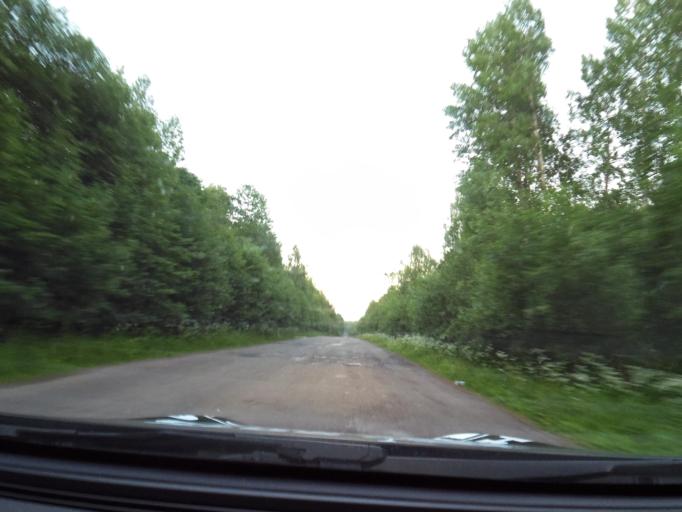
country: RU
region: Leningrad
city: Voznesen'ye
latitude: 60.8420
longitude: 35.6276
